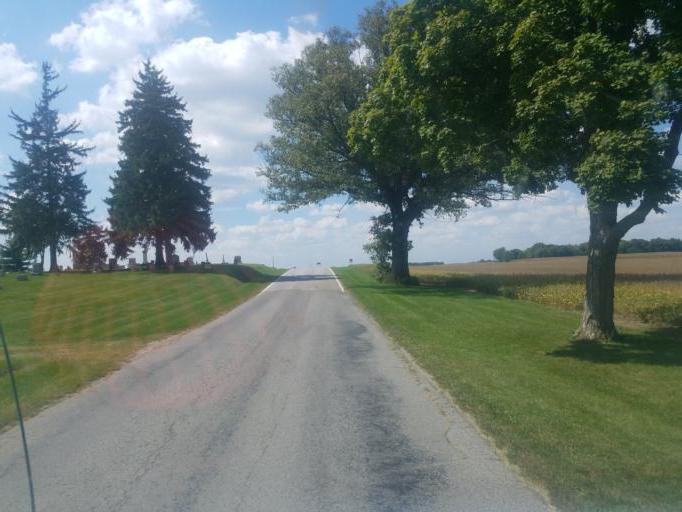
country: US
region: Ohio
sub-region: Hardin County
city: Ada
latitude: 40.6539
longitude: -83.8973
